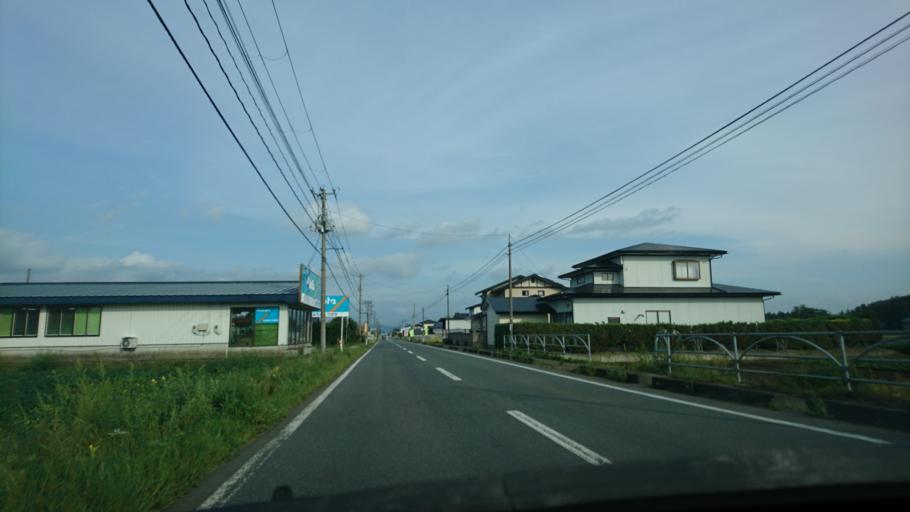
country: JP
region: Iwate
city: Kitakami
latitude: 39.3046
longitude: 141.0137
